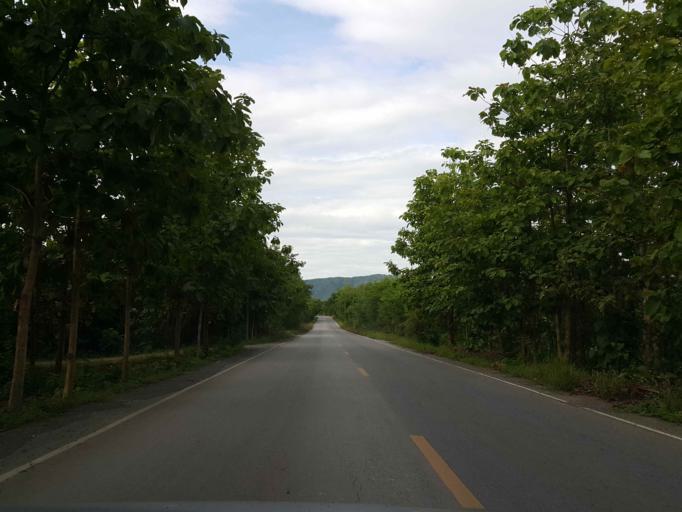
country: TH
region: Sukhothai
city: Thung Saliam
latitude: 17.2482
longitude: 99.5182
